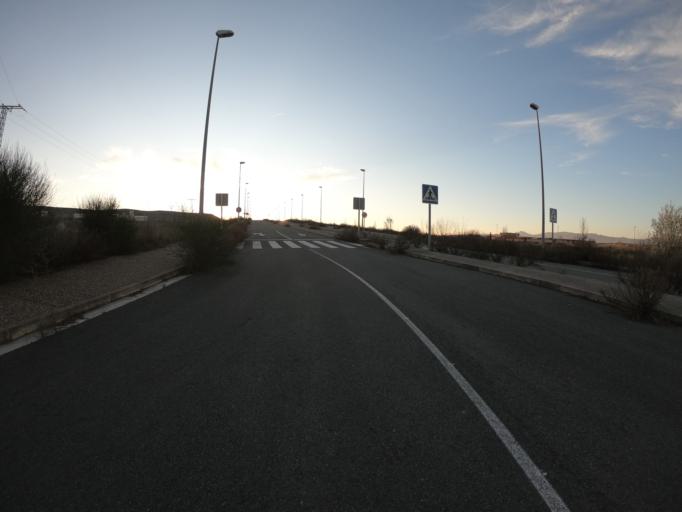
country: ES
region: Basque Country
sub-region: Provincia de Alava
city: Oyon
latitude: 42.4863
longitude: -2.4171
